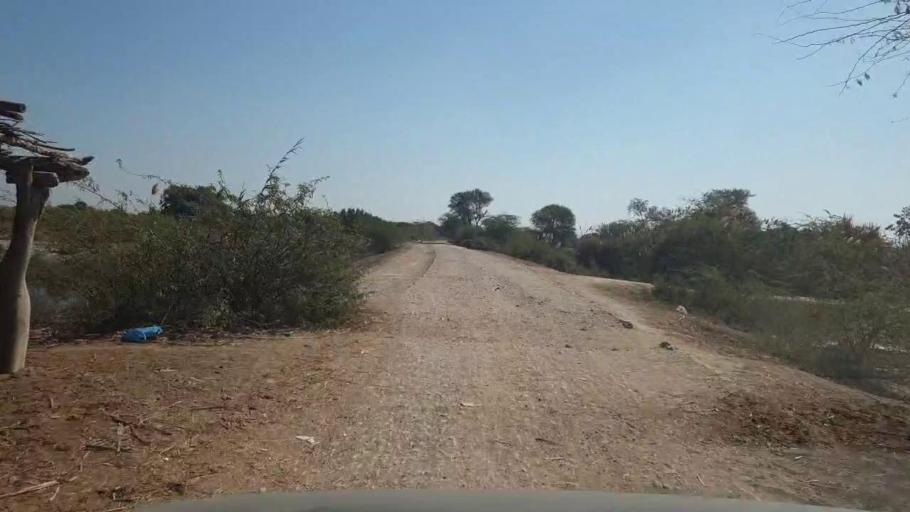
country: PK
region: Sindh
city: Mirwah Gorchani
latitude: 25.3033
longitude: 69.1195
